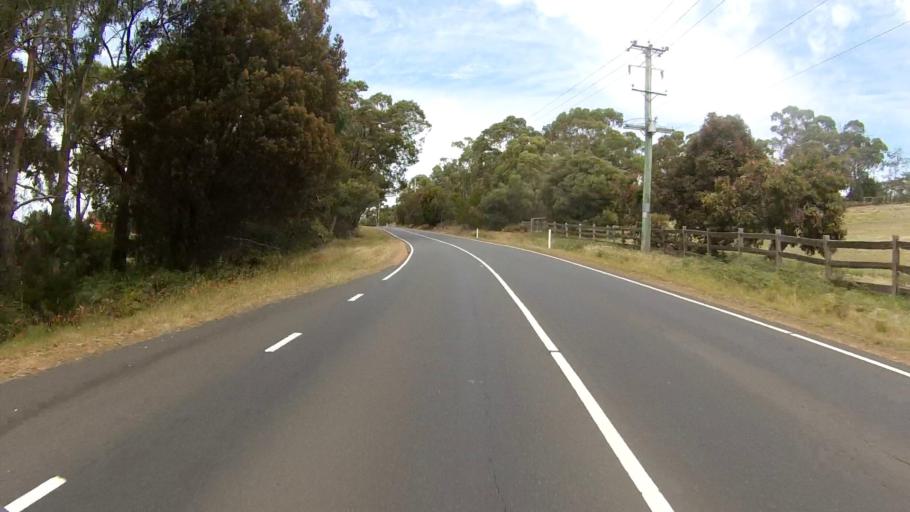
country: AU
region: Tasmania
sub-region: Clarence
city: Acton Park
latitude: -42.8789
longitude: 147.4819
